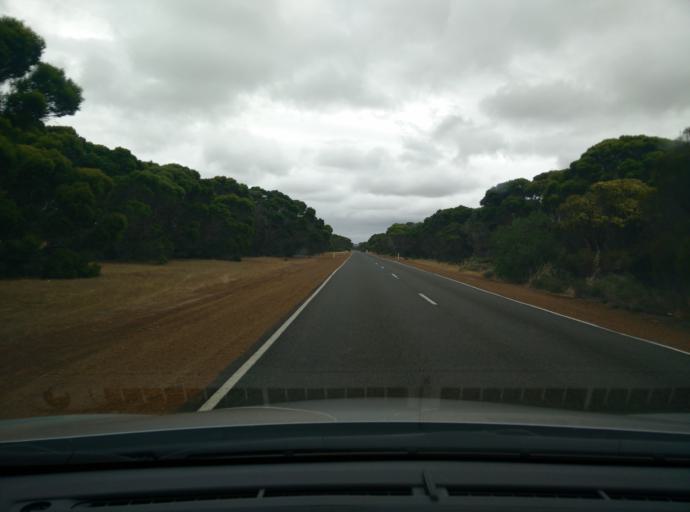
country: AU
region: South Australia
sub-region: Kangaroo Island
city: Kingscote
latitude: -35.7037
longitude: 137.5680
